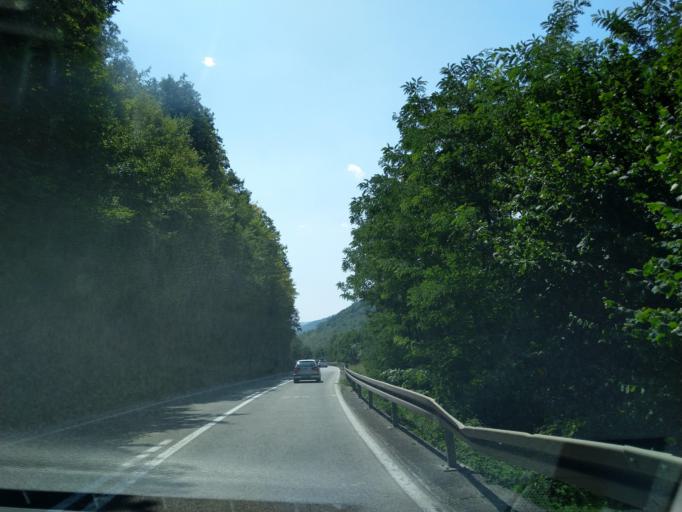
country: RS
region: Central Serbia
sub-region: Zlatiborski Okrug
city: Prijepolje
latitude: 43.4600
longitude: 19.6464
